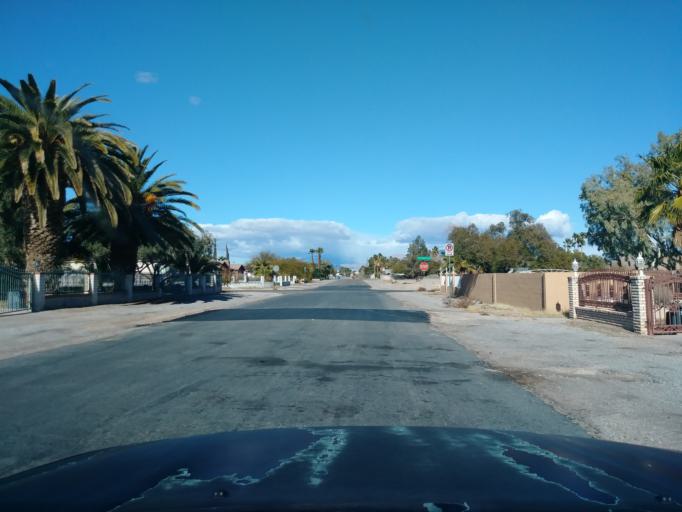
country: US
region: Nevada
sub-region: Clark County
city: Spring Valley
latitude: 36.1475
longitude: -115.2232
